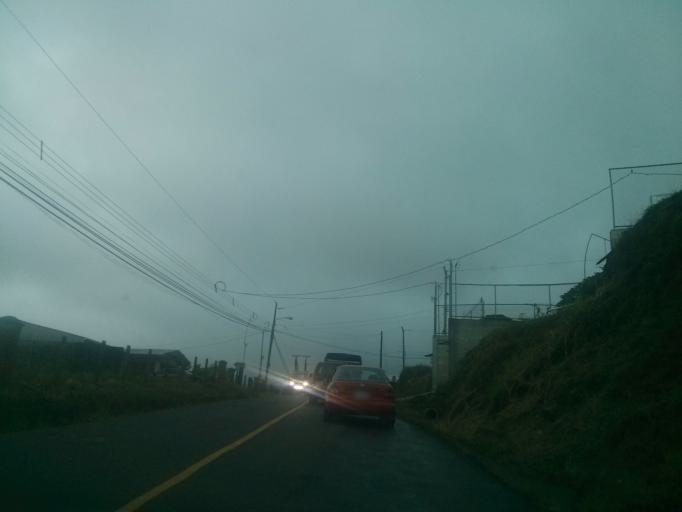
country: CR
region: Cartago
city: Cot
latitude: 9.9127
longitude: -83.8028
